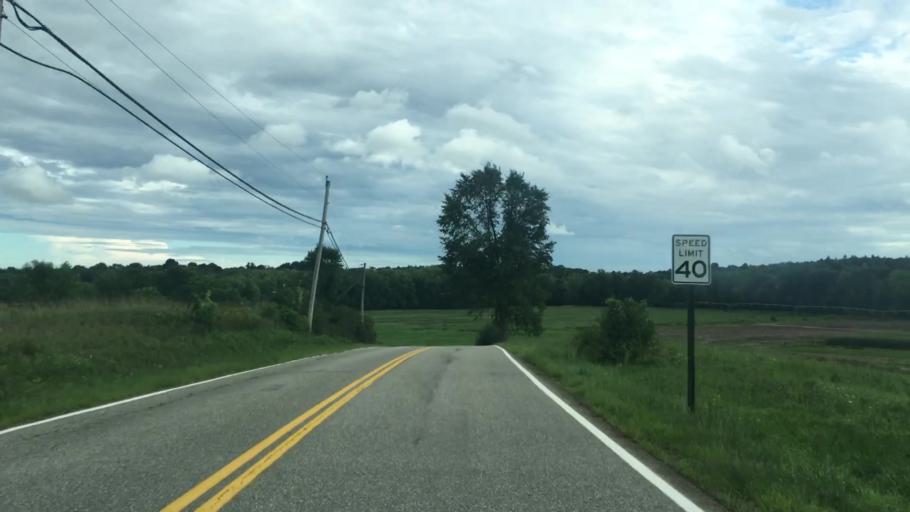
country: US
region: Maine
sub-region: York County
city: Biddeford
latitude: 43.5044
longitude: -70.5040
